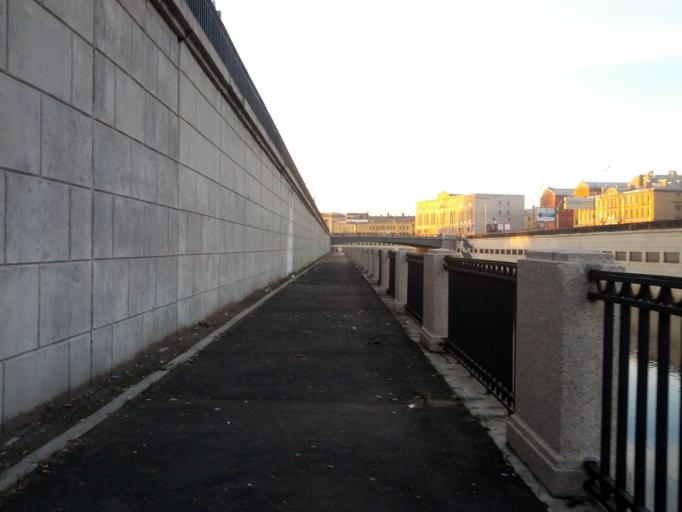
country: RU
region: St.-Petersburg
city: Centralniy
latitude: 59.9155
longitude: 30.3482
